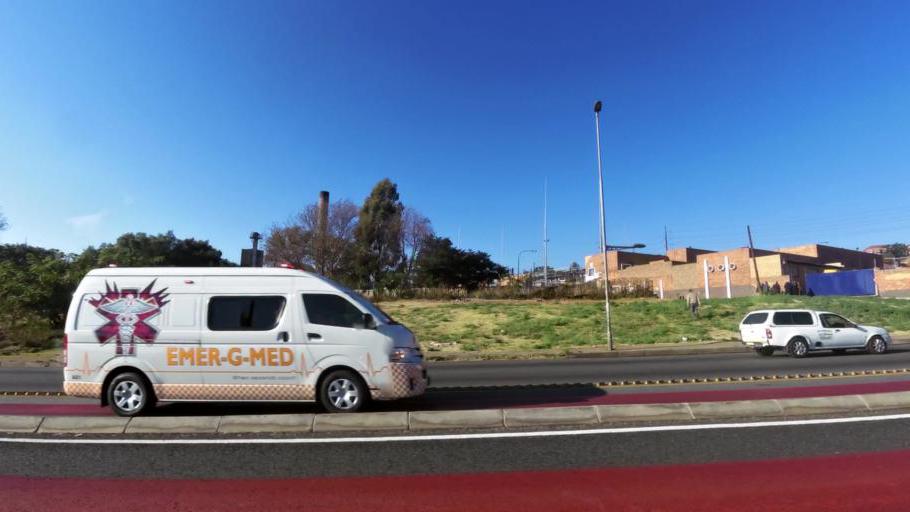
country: ZA
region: Gauteng
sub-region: City of Johannesburg Metropolitan Municipality
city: Johannesburg
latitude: -26.1856
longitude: 27.9850
